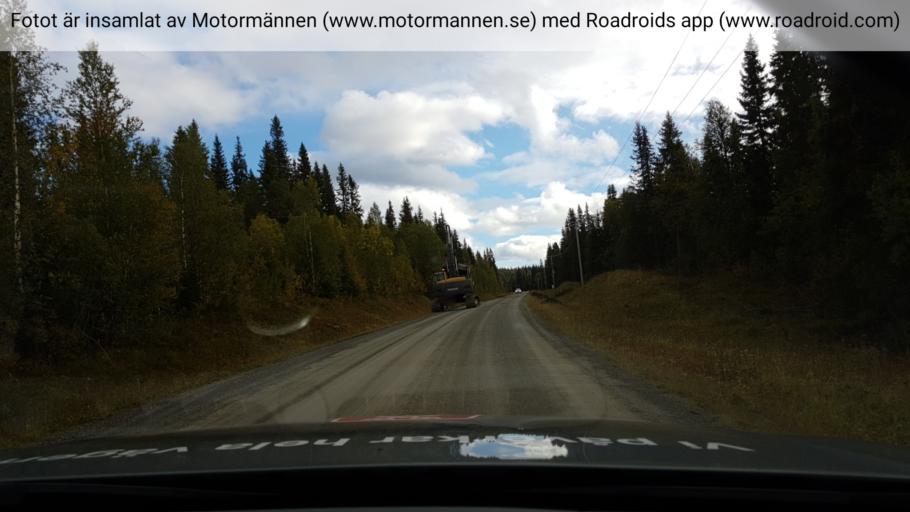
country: SE
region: Jaemtland
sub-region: Are Kommun
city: Are
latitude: 63.7058
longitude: 12.7446
